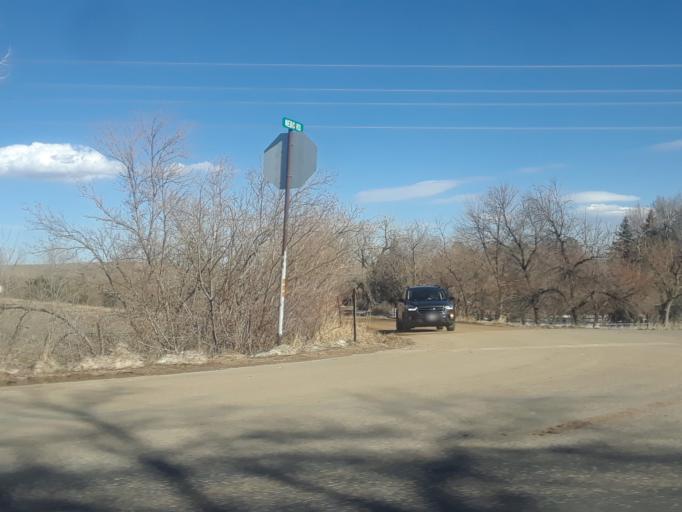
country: US
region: Colorado
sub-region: Boulder County
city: Boulder
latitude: 40.1146
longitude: -105.2823
